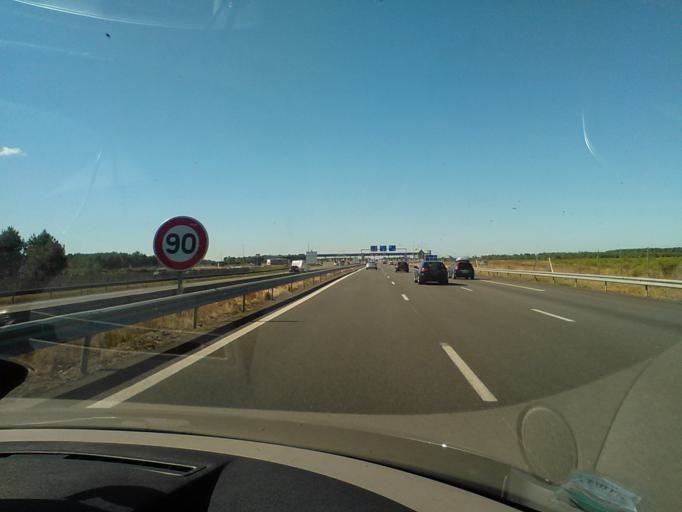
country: FR
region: Aquitaine
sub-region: Departement des Landes
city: Pissos
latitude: 44.3520
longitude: -0.8571
